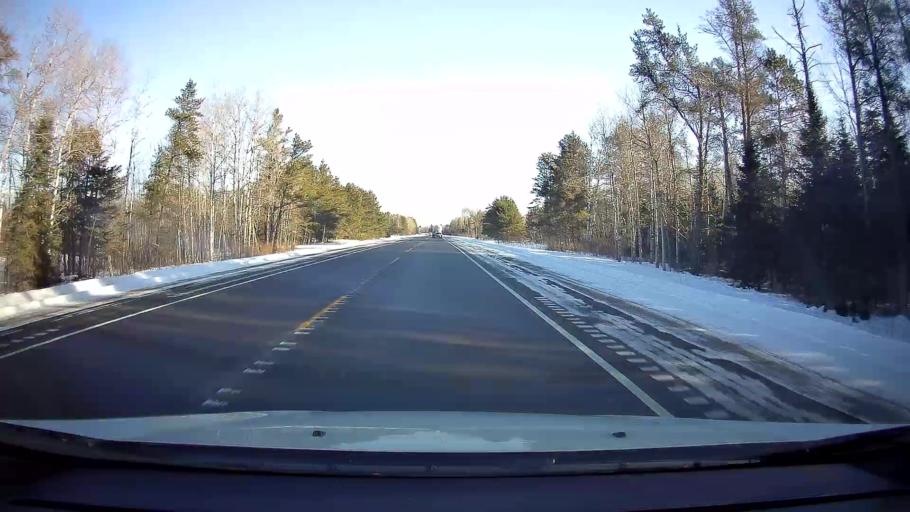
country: US
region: Wisconsin
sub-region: Sawyer County
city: Hayward
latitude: 46.0880
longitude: -91.3931
